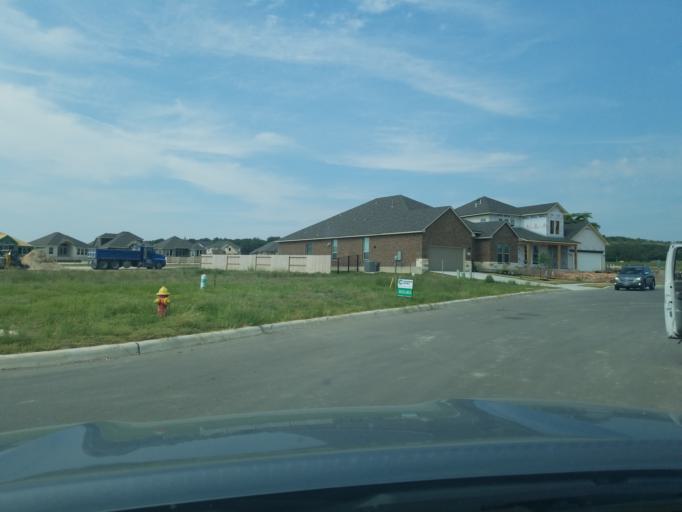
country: US
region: Texas
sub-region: Kendall County
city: Boerne
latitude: 29.7546
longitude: -98.7145
